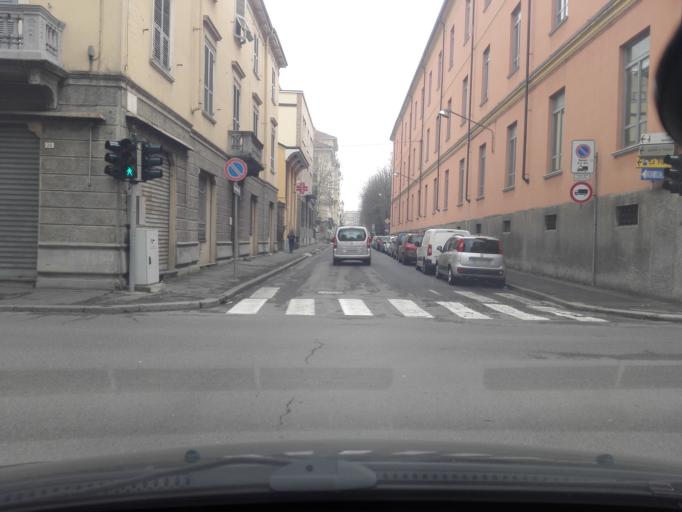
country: IT
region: Piedmont
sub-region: Provincia di Alessandria
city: Novi Ligure
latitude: 44.7658
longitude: 8.7872
